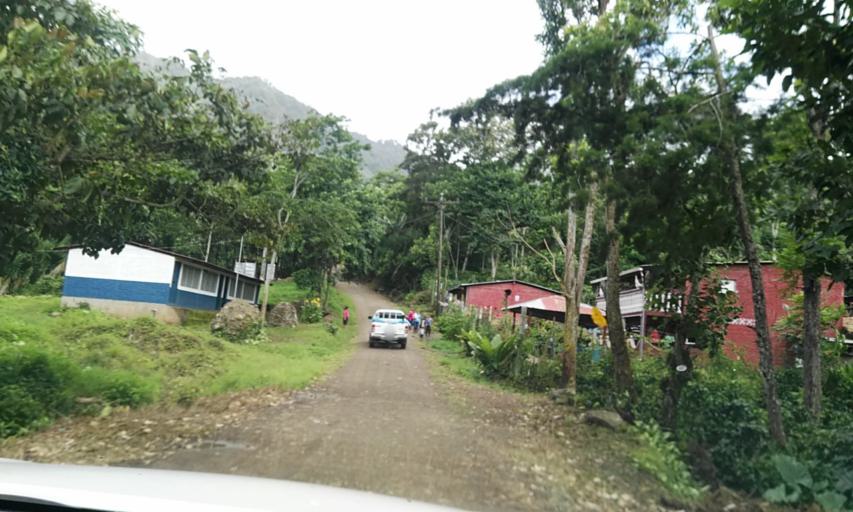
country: NI
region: Matagalpa
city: San Ramon
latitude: 13.0074
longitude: -85.8732
